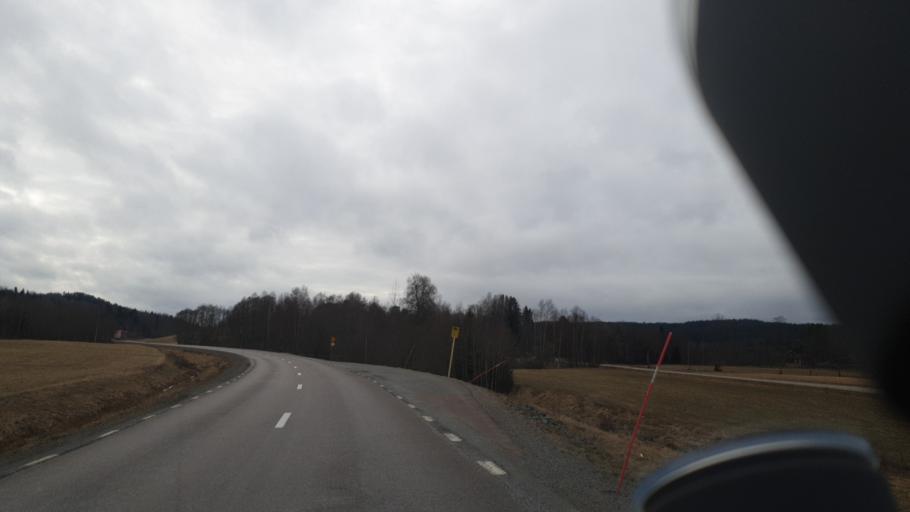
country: SE
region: Vaermland
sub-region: Arjangs Kommun
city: Arjaeng
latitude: 59.6358
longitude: 12.1352
